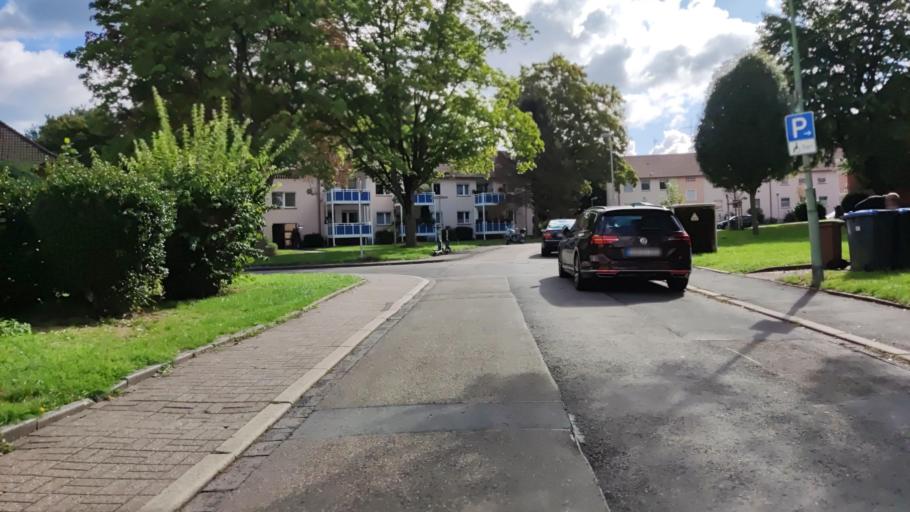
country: DE
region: North Rhine-Westphalia
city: Bochum-Hordel
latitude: 51.5185
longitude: 7.1854
